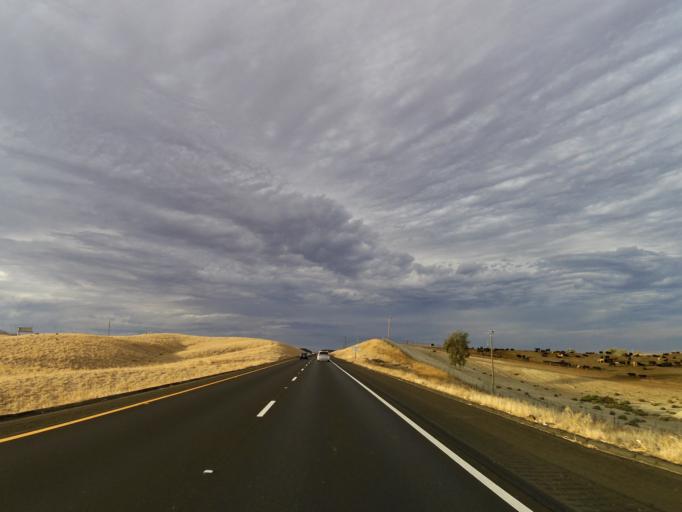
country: US
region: California
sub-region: Fresno County
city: Coalinga
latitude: 36.3084
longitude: -120.2797
